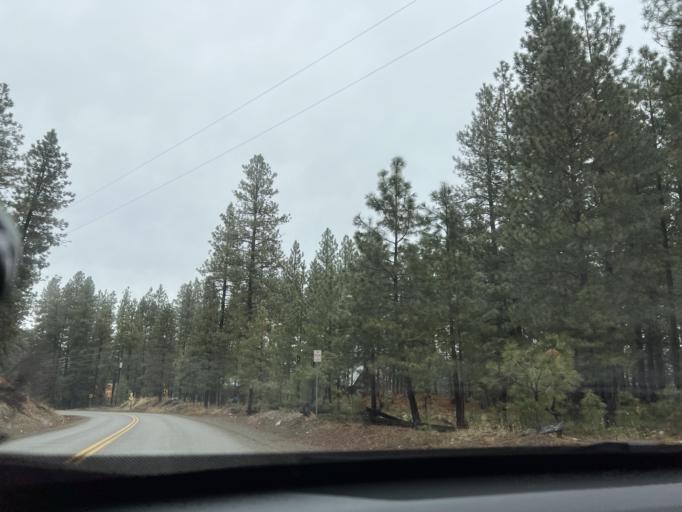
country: US
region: Washington
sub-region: Okanogan County
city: Brewster
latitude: 48.4650
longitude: -120.2076
